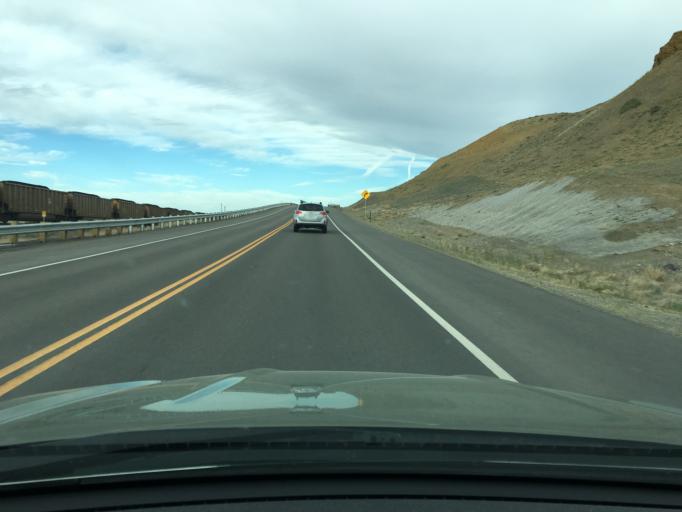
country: US
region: Colorado
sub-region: Delta County
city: Cedaredge
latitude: 38.7978
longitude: -107.8246
